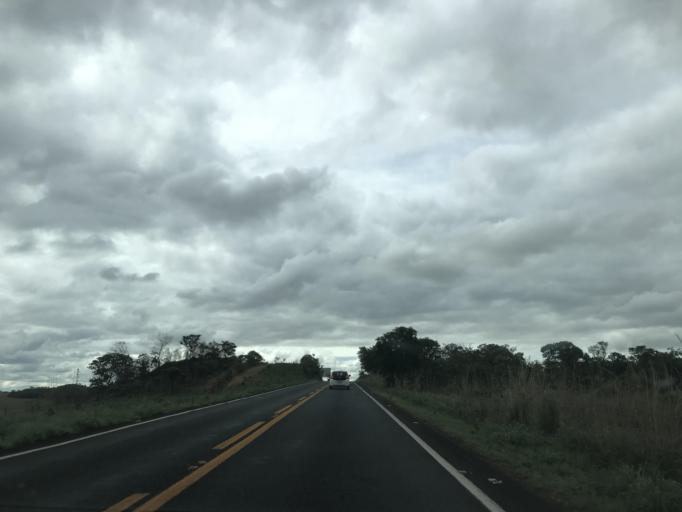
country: BR
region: Goias
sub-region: Caldas Novas
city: Caldas Novas
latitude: -17.5870
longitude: -48.7289
